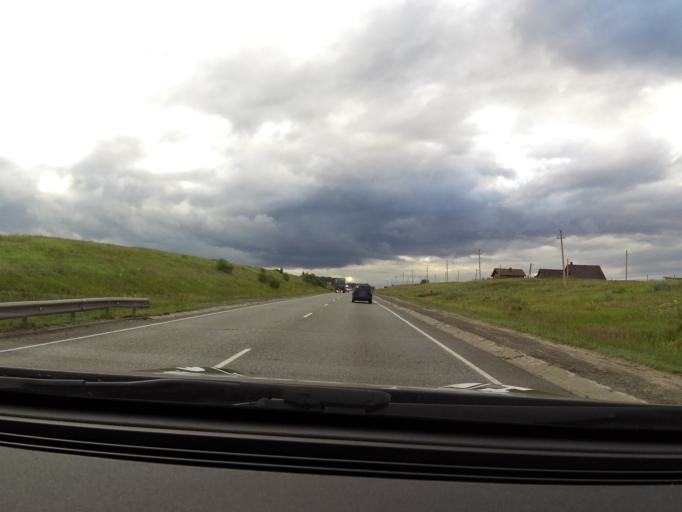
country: RU
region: Tatarstan
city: Sviyazhsk
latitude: 55.7119
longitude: 48.6477
